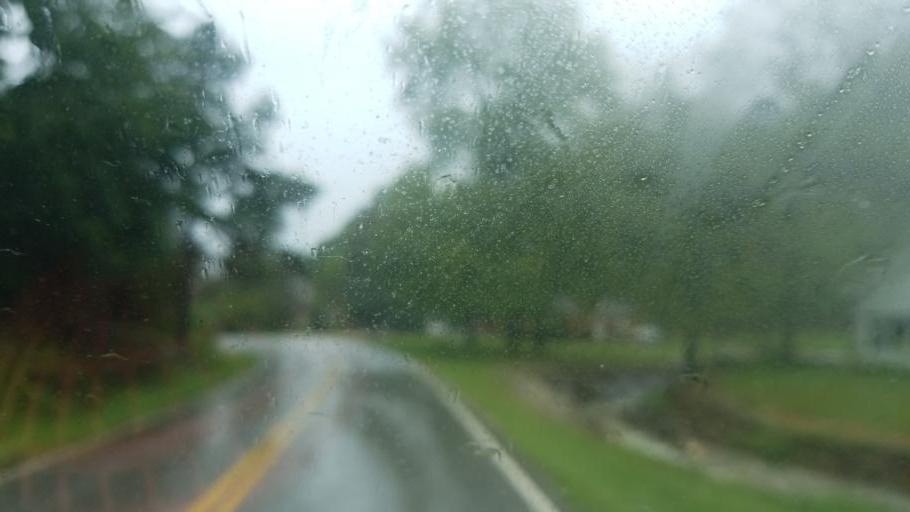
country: US
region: Ohio
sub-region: Scioto County
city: Franklin Furnace
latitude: 38.6455
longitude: -82.9269
